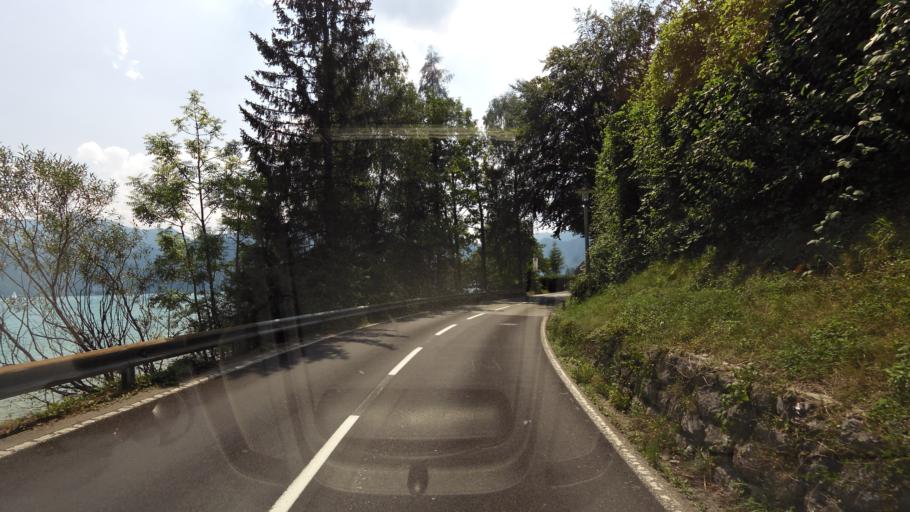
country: AT
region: Upper Austria
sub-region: Politischer Bezirk Vocklabruck
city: Steinbach am Attersee
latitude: 47.8278
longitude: 13.5170
